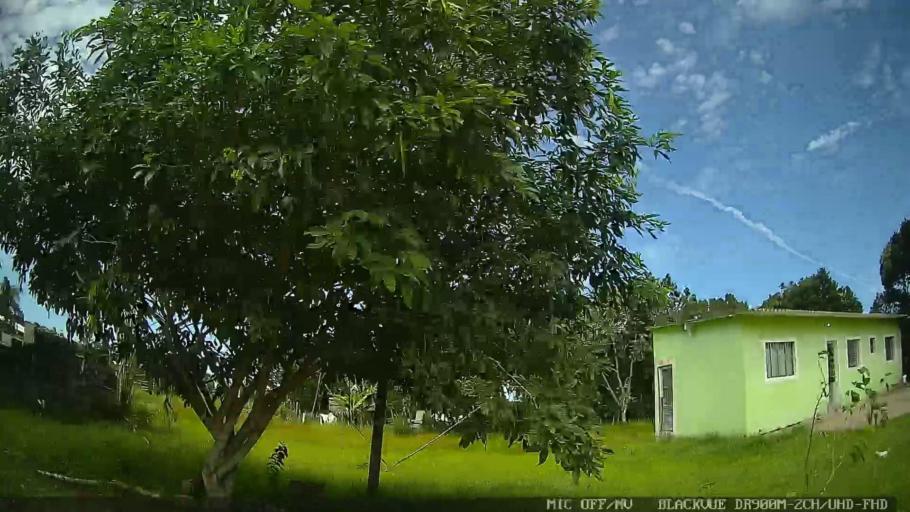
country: BR
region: Sao Paulo
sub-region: Iguape
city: Iguape
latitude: -24.7192
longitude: -47.5255
